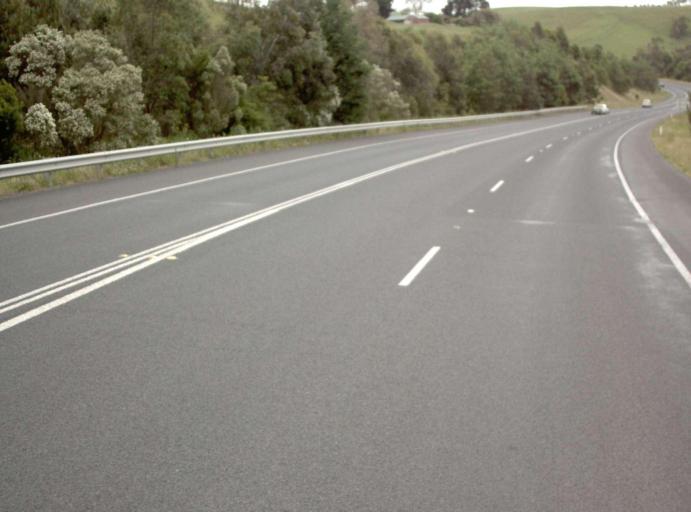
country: AU
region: Victoria
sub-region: Bass Coast
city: North Wonthaggi
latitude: -38.3823
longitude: 145.7360
